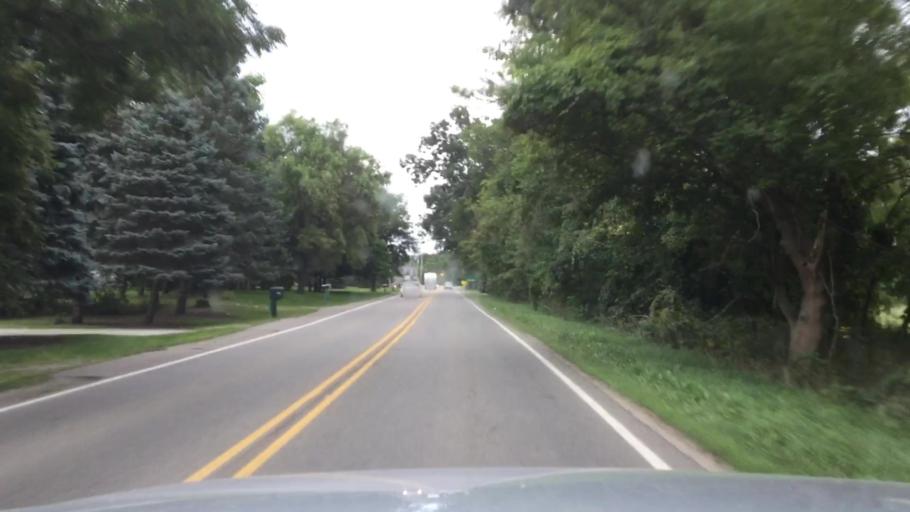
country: US
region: Michigan
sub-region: Genesee County
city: Argentine
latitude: 42.7925
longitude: -83.8510
